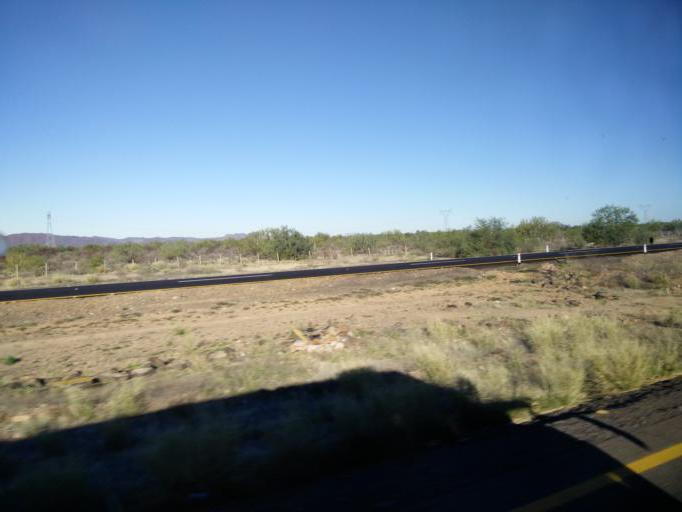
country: MX
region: Sonora
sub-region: Empalme
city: Empalme
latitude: 28.3480
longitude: -111.0424
